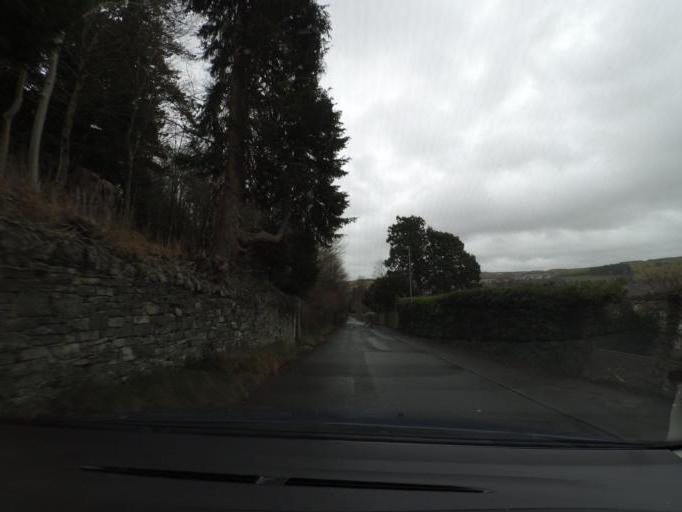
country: GB
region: Scotland
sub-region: The Scottish Borders
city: Hawick
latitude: 55.4241
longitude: -2.8001
